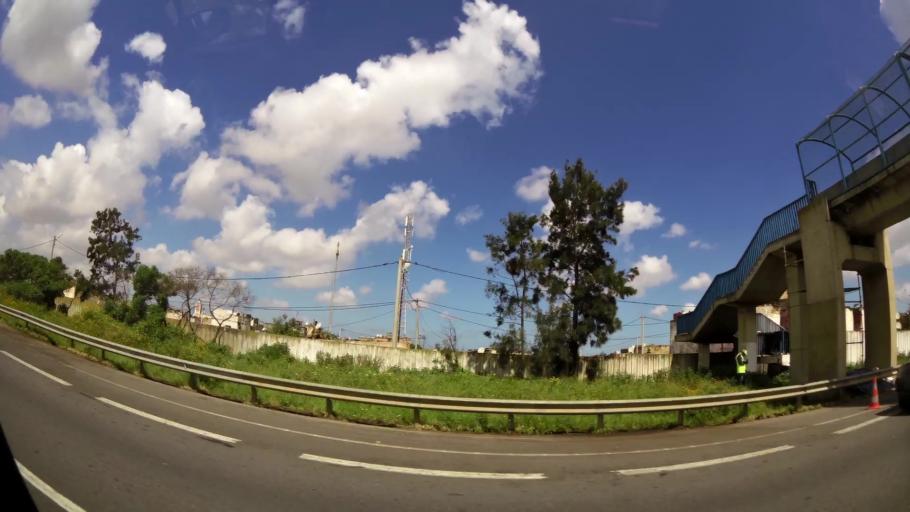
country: MA
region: Grand Casablanca
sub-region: Mediouna
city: Tit Mellil
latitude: 33.5409
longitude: -7.5352
